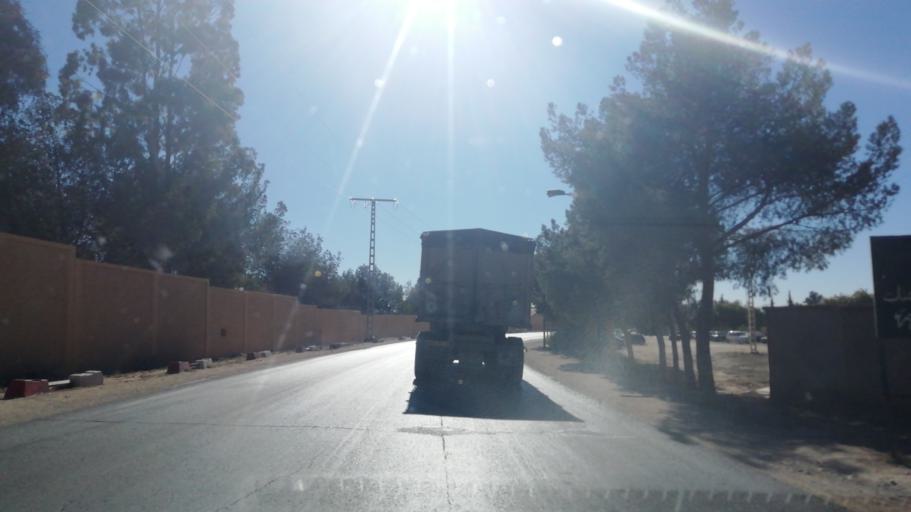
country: DZ
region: Saida
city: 'Ain el Hadjar
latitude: 34.1453
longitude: 0.0714
